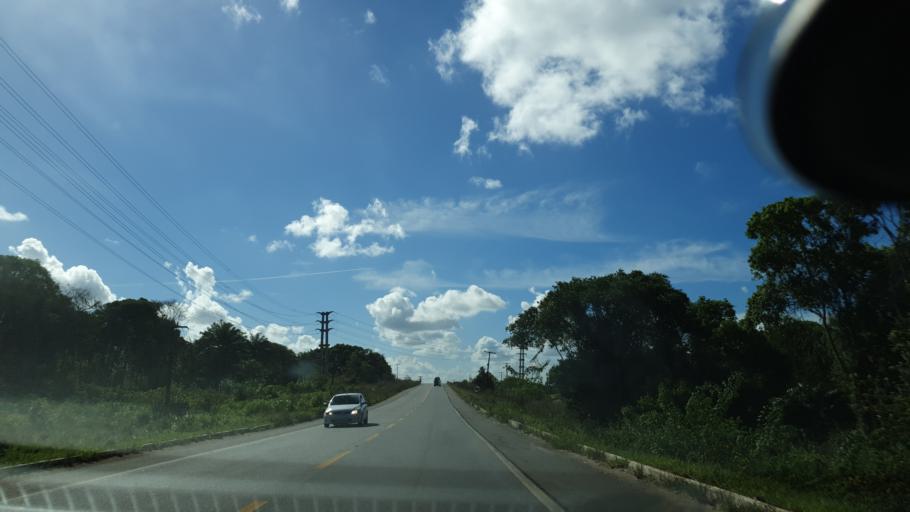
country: BR
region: Bahia
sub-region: Camacari
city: Camacari
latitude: -12.6827
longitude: -38.2371
